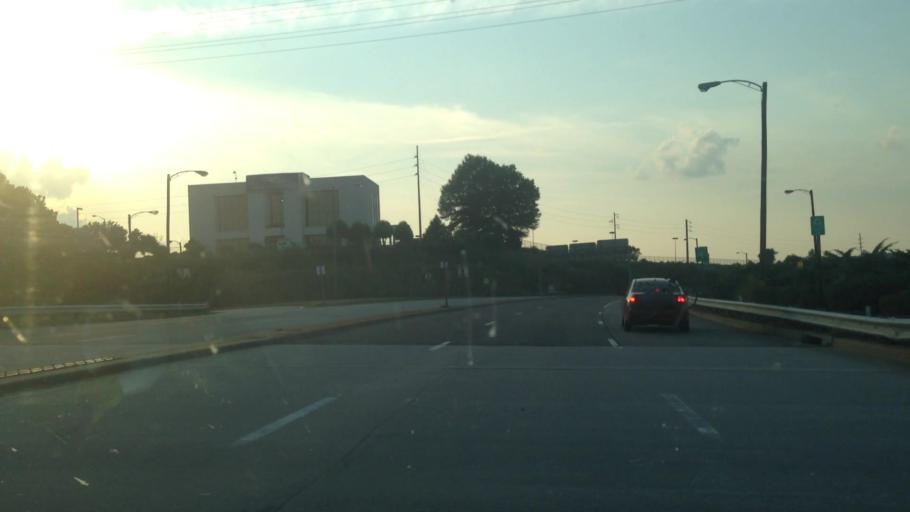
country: US
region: Virginia
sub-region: City of Danville
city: Danville
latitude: 36.5921
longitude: -79.4167
